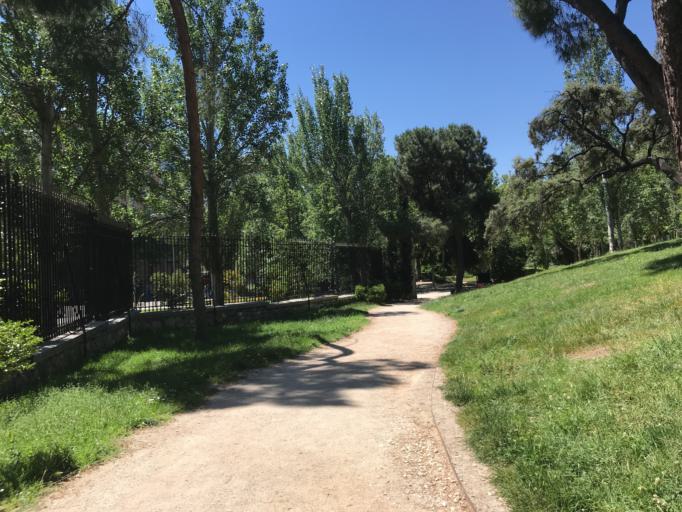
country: ES
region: Madrid
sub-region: Provincia de Madrid
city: Retiro
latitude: 40.4118
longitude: -3.6767
